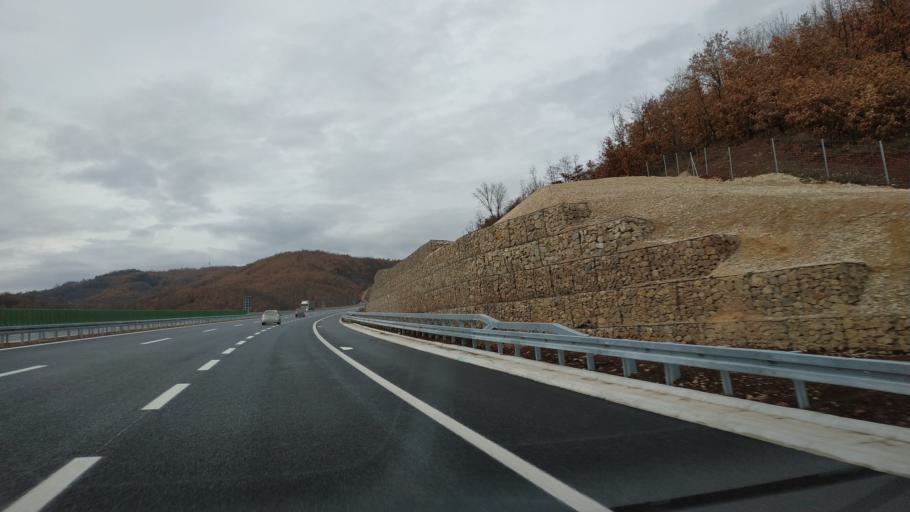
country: RS
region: Central Serbia
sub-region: Nisavski Okrug
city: Gadzin Han
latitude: 43.2600
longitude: 22.1464
